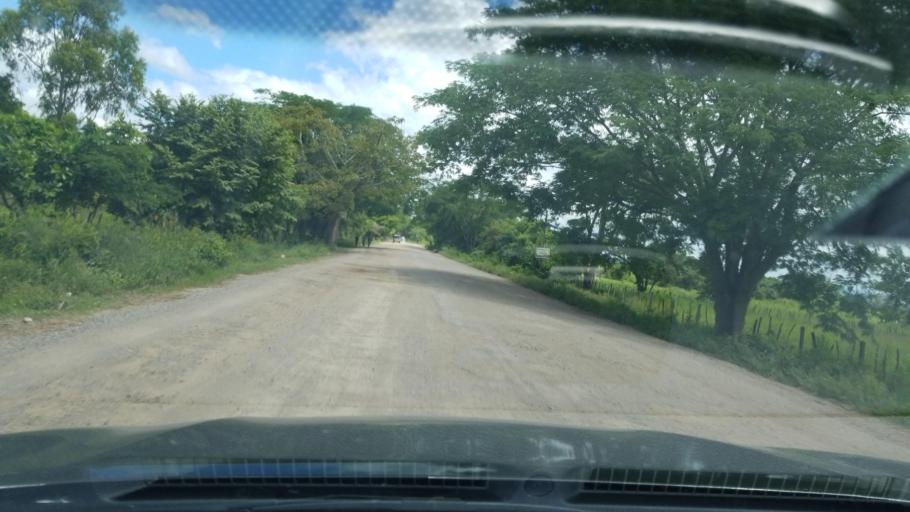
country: HN
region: Francisco Morazan
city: Talanga
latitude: 14.3743
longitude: -87.0623
